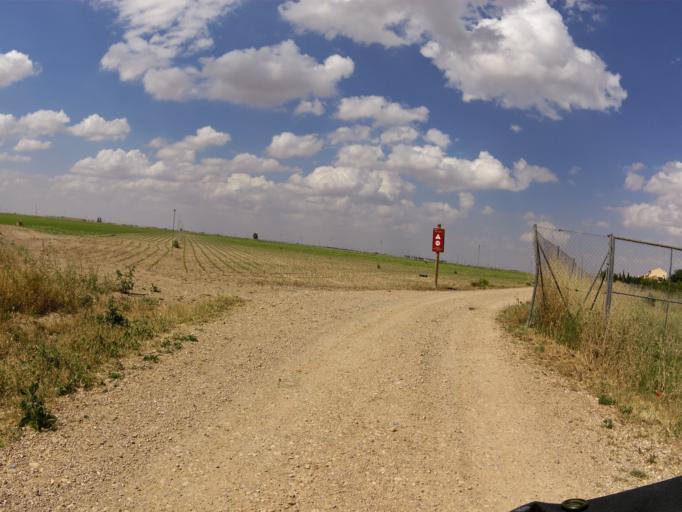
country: ES
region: Castille-La Mancha
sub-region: Provincia de Albacete
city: Pozuelo
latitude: 38.9160
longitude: -2.0115
